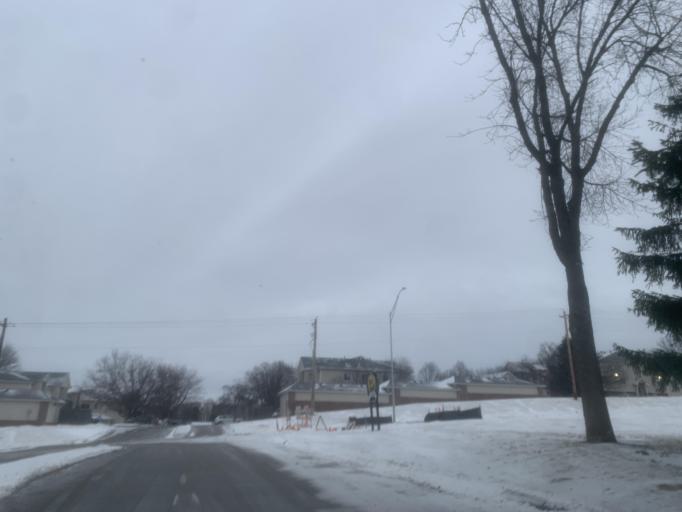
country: US
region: Nebraska
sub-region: Douglas County
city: Ralston
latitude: 41.2723
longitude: -96.0819
